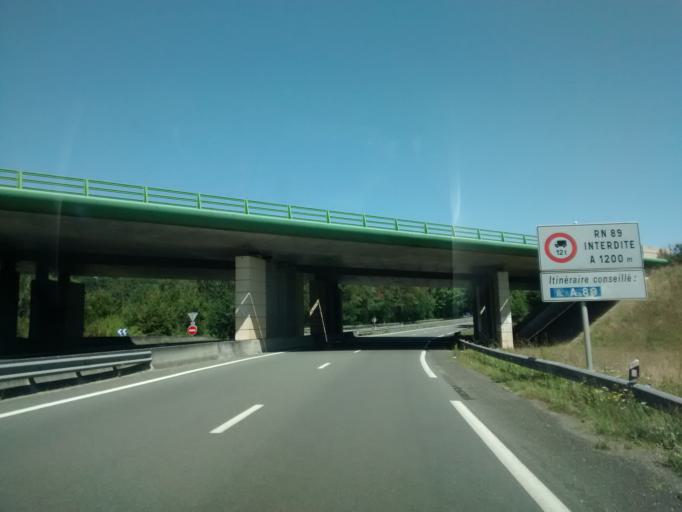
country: FR
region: Aquitaine
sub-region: Departement de la Gironde
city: Abzac
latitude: 45.0068
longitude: -0.1166
